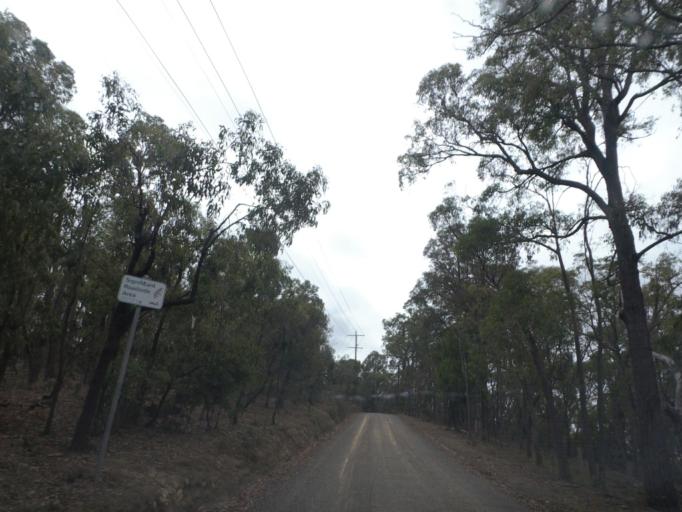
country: AU
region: Victoria
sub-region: Yarra Ranges
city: Chirnside Park
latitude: -37.6919
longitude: 145.2950
